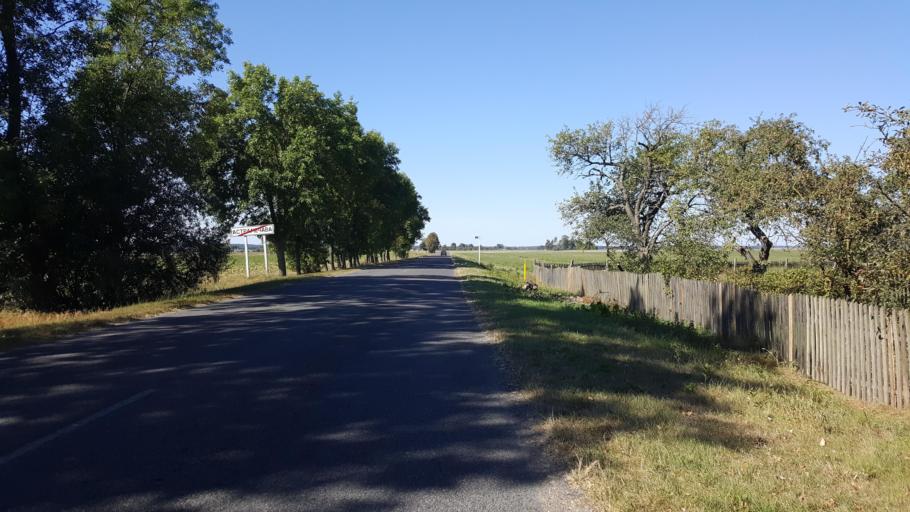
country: BY
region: Brest
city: Charnawchytsy
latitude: 52.2615
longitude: 23.5588
